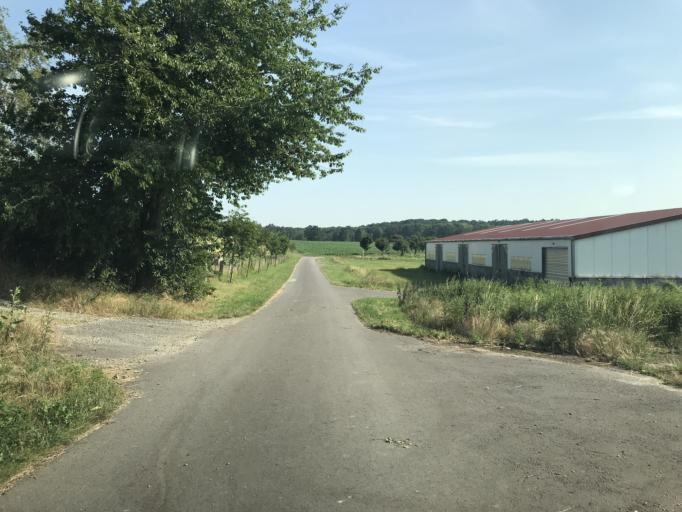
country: DE
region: Saxony-Anhalt
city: Beendorf
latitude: 52.2468
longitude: 11.1343
